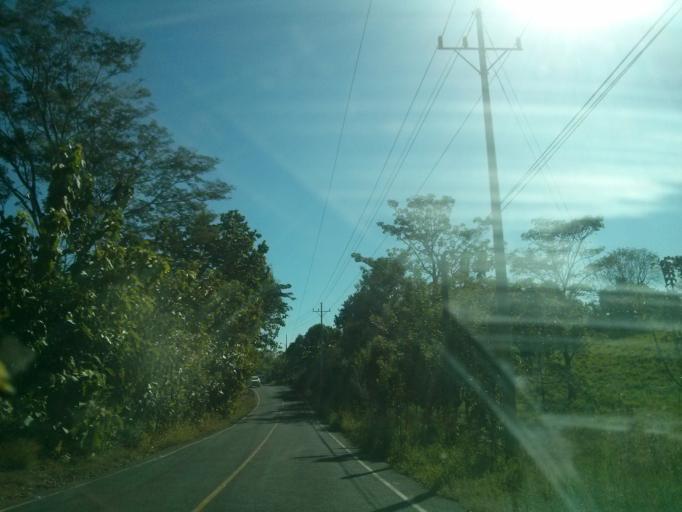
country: CR
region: Puntarenas
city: Paquera
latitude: 9.7016
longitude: -85.0322
